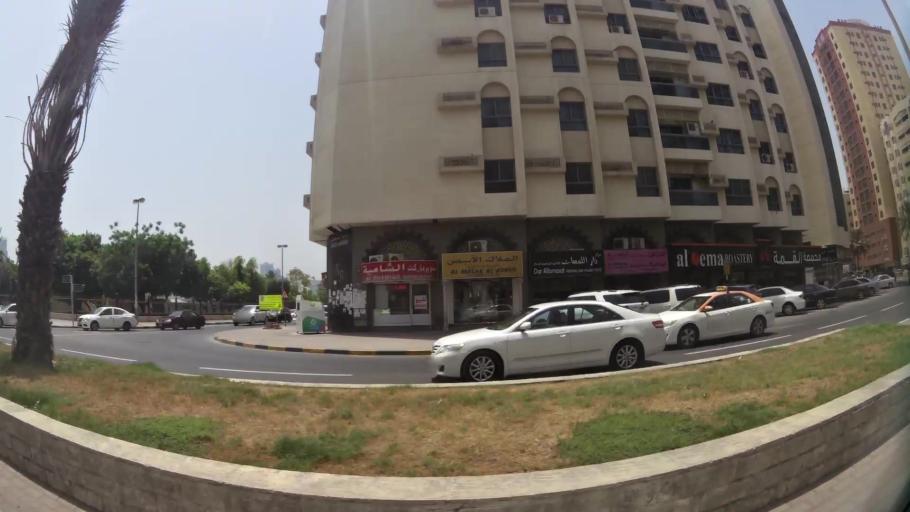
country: AE
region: Ash Shariqah
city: Sharjah
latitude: 25.3284
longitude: 55.3930
